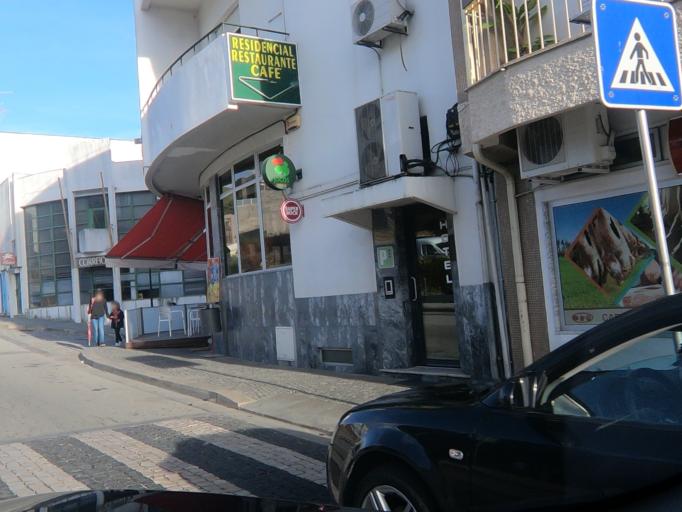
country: PT
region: Vila Real
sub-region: Santa Marta de Penaguiao
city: Santa Marta de Penaguiao
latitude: 41.2109
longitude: -7.7869
